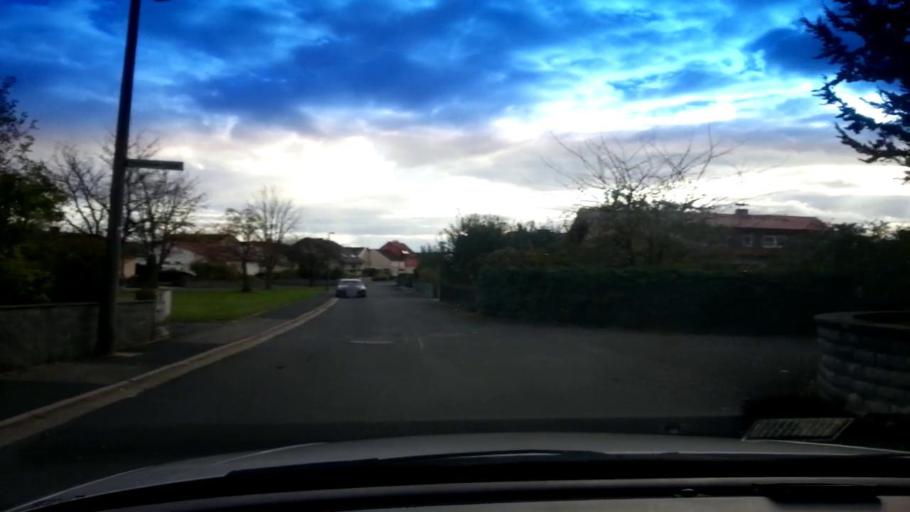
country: DE
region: Bavaria
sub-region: Upper Franconia
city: Rattelsdorf
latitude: 50.0096
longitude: 10.9028
